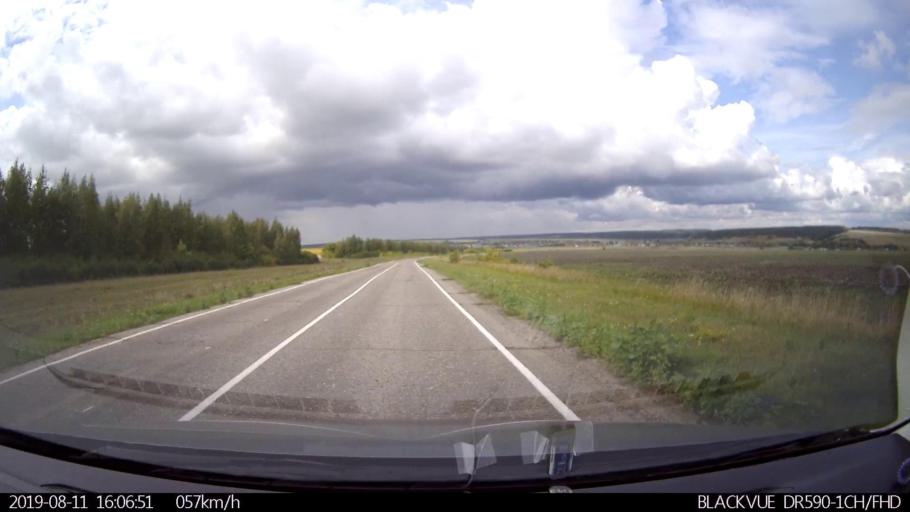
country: RU
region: Ulyanovsk
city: Ignatovka
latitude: 53.9720
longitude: 47.6470
